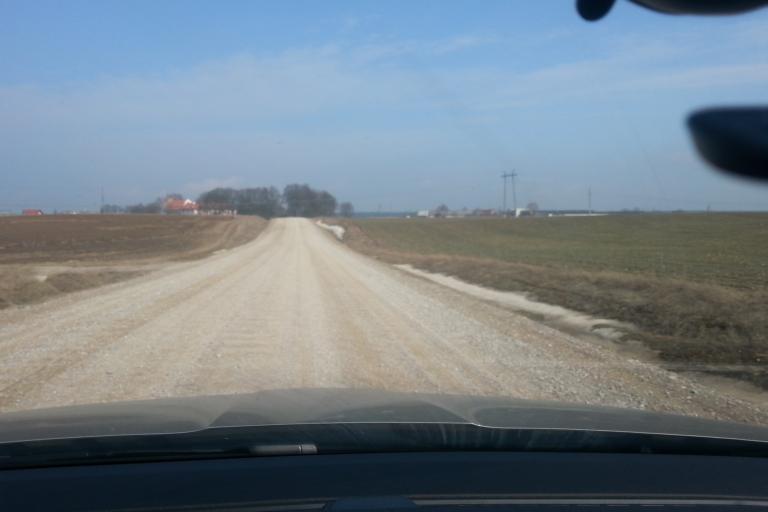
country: LT
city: Trakai
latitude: 54.6008
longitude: 24.9813
